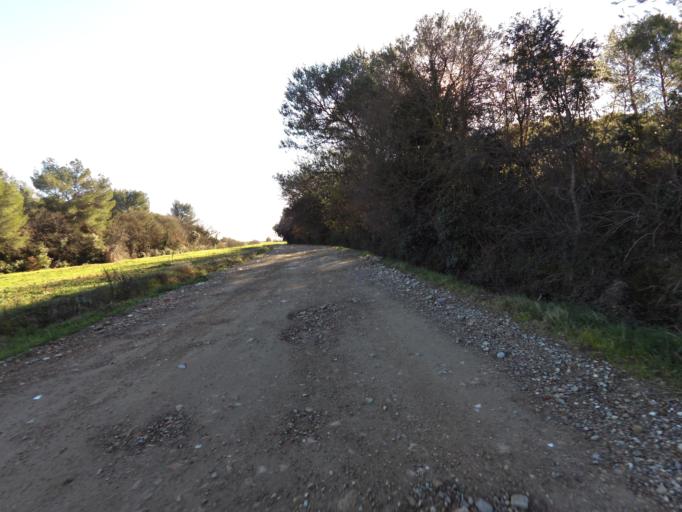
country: FR
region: Languedoc-Roussillon
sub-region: Departement du Gard
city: Aigues-Vives
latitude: 43.7317
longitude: 4.1706
